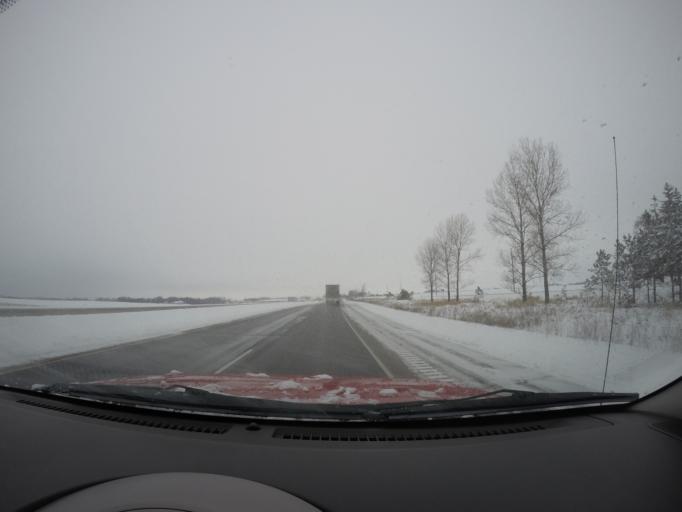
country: US
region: Minnesota
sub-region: Winona County
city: Lewiston
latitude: 43.9398
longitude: -91.7735
